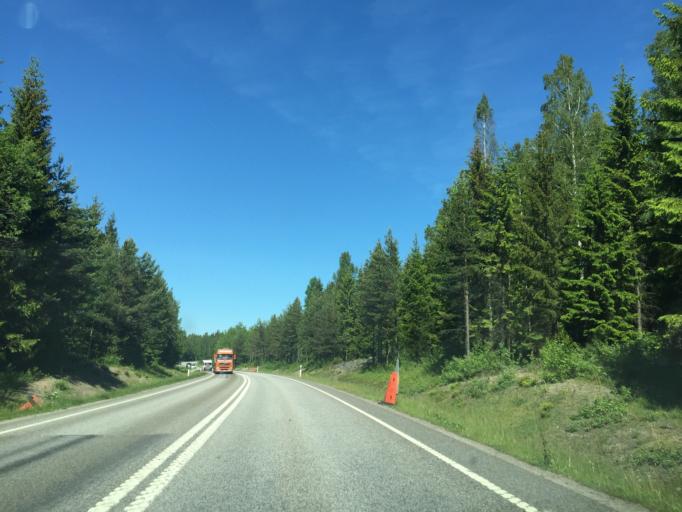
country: SE
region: OEstergoetland
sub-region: Motala Kommun
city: Ryd
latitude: 58.6602
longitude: 14.9644
